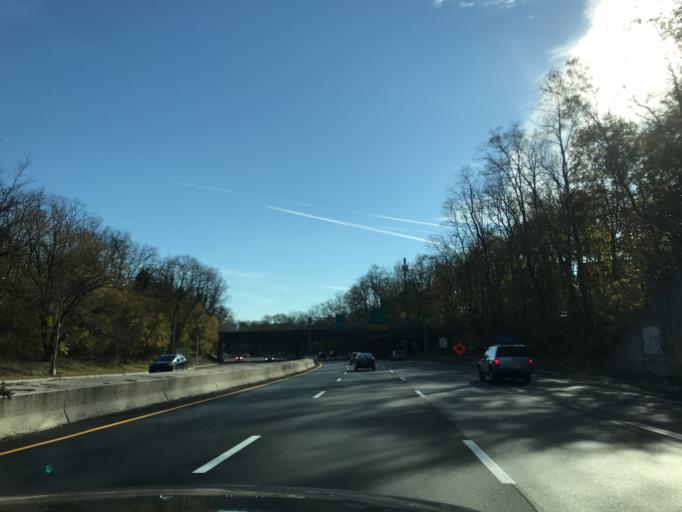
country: US
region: New Jersey
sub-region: Essex County
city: Orange
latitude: 40.7758
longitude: -74.2417
